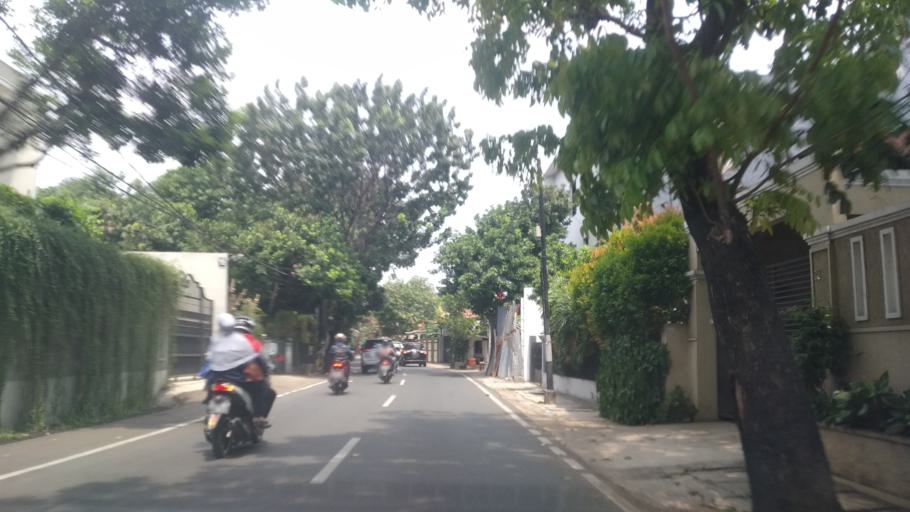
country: ID
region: Banten
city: South Tangerang
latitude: -6.2507
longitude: 106.7738
